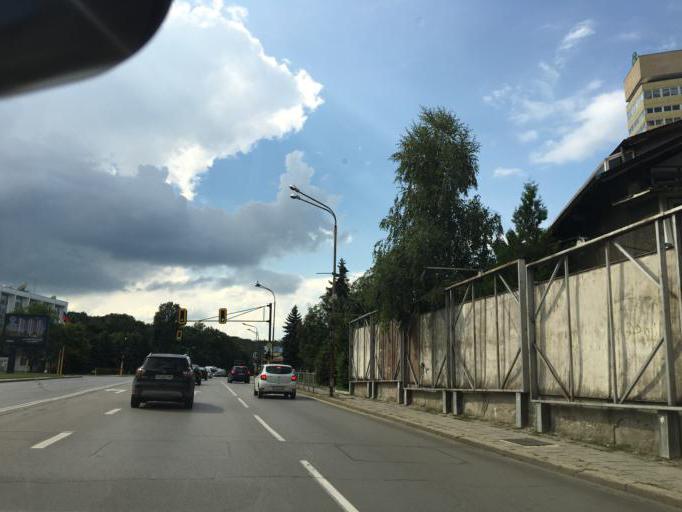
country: BG
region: Sofia-Capital
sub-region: Stolichna Obshtina
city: Sofia
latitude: 42.6724
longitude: 23.3492
